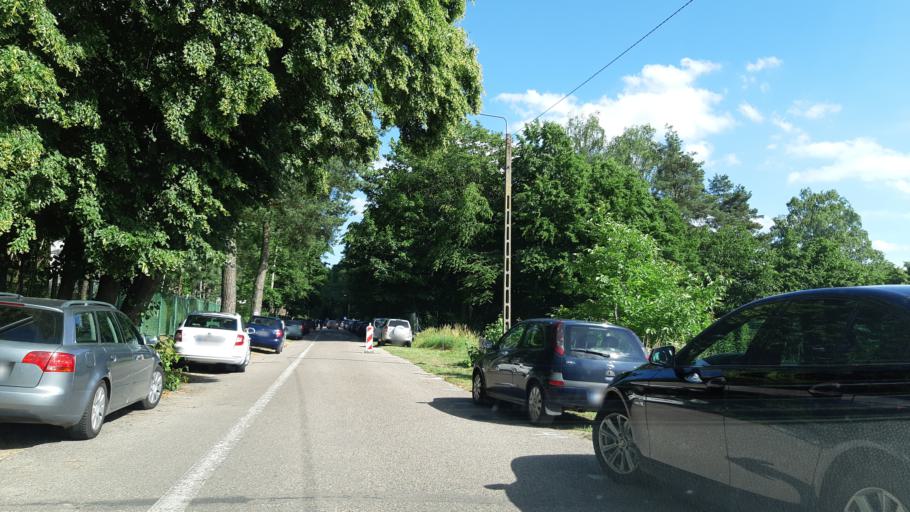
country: PL
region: Warmian-Masurian Voivodeship
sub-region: Powiat mragowski
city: Mragowo
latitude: 53.8748
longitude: 21.3188
